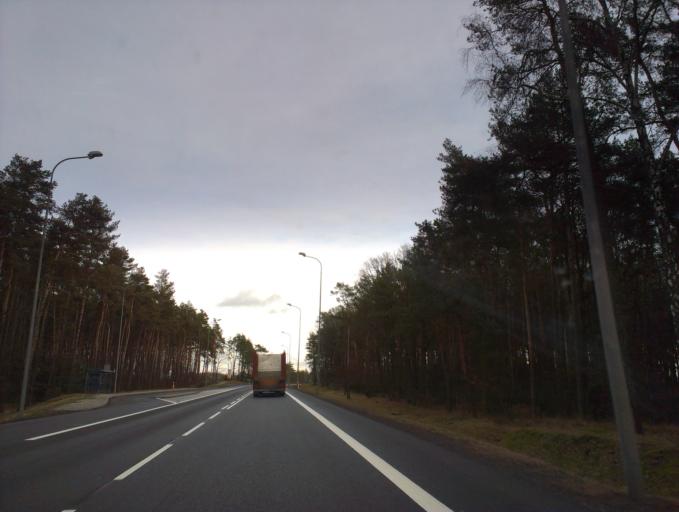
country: PL
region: Kujawsko-Pomorskie
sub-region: Powiat lipnowski
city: Skepe
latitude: 52.8865
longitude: 19.3969
